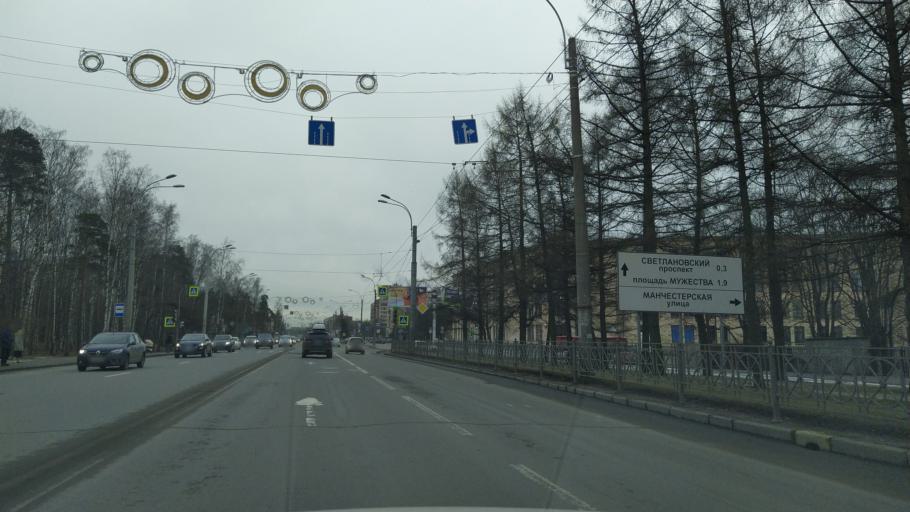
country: RU
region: St.-Petersburg
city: Sosnovka
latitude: 60.0137
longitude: 30.3424
